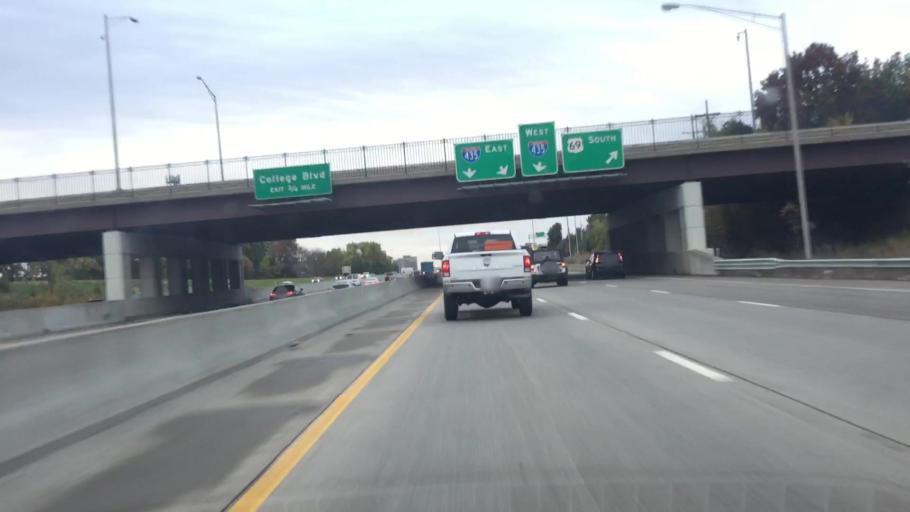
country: US
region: Kansas
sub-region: Johnson County
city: Lenexa
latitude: 38.9405
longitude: -94.7064
